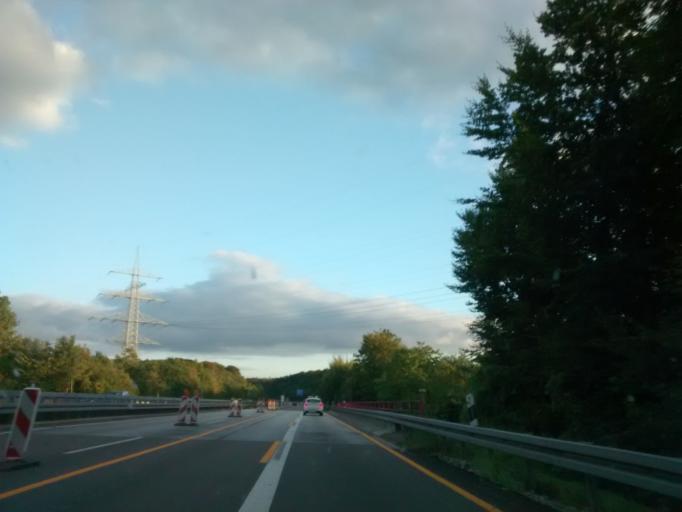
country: DE
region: Lower Saxony
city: Osnabrueck
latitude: 52.2545
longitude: 8.0164
